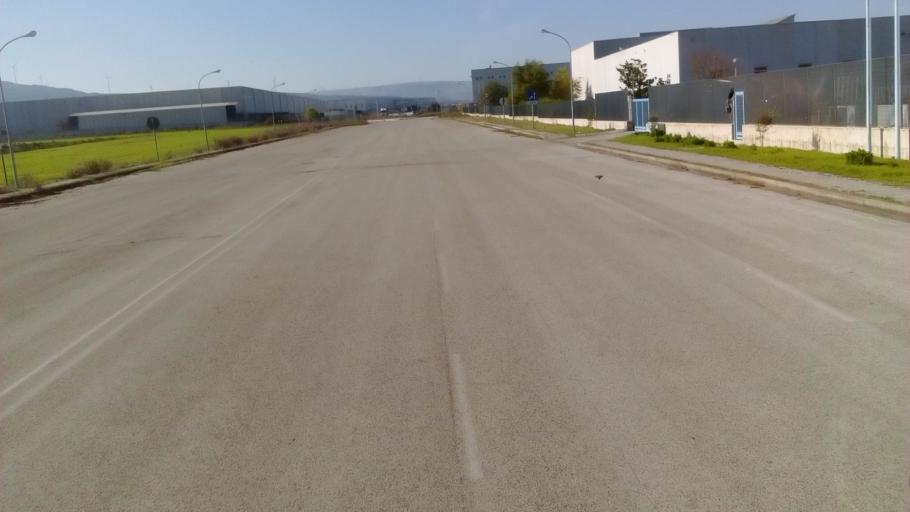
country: IT
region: Basilicate
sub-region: Provincia di Potenza
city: Melfi
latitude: 41.0782
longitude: 15.6629
